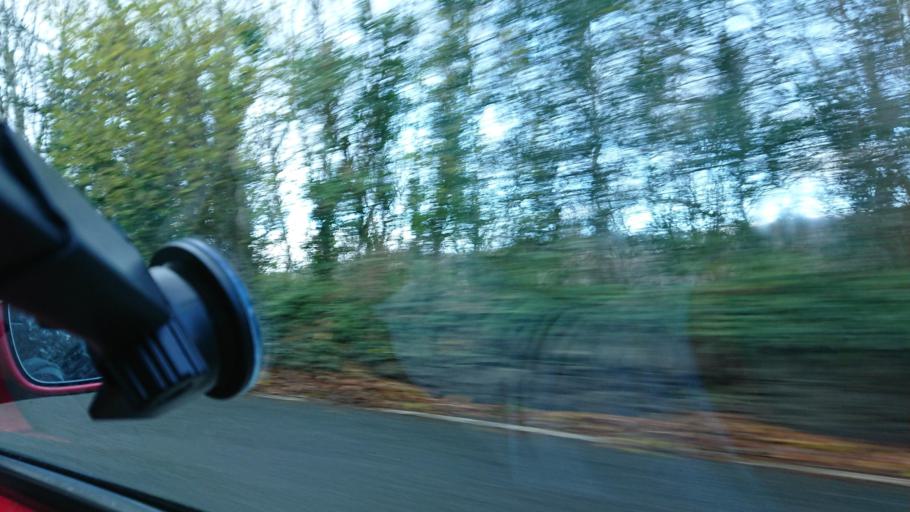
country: GB
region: England
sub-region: Cornwall
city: Looe
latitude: 50.3551
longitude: -4.4670
